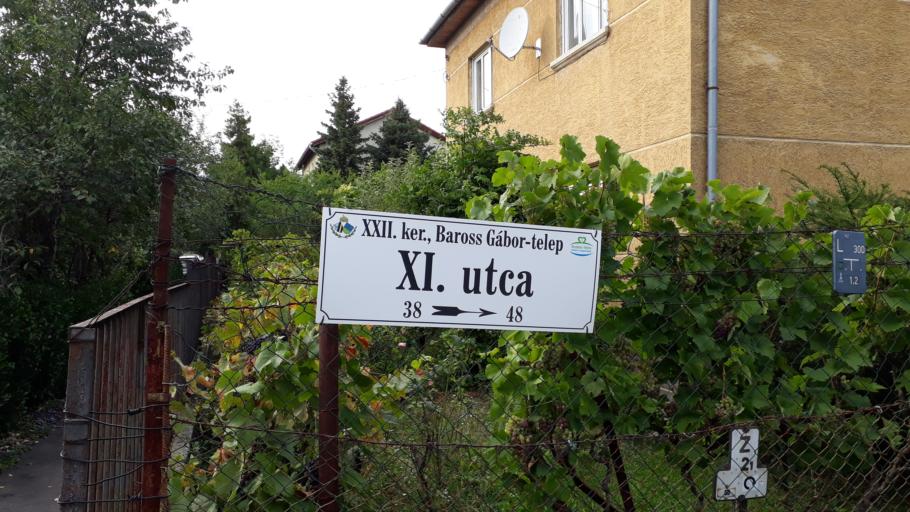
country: HU
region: Budapest
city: Budapest XXII. keruelet
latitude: 47.4125
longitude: 18.9989
